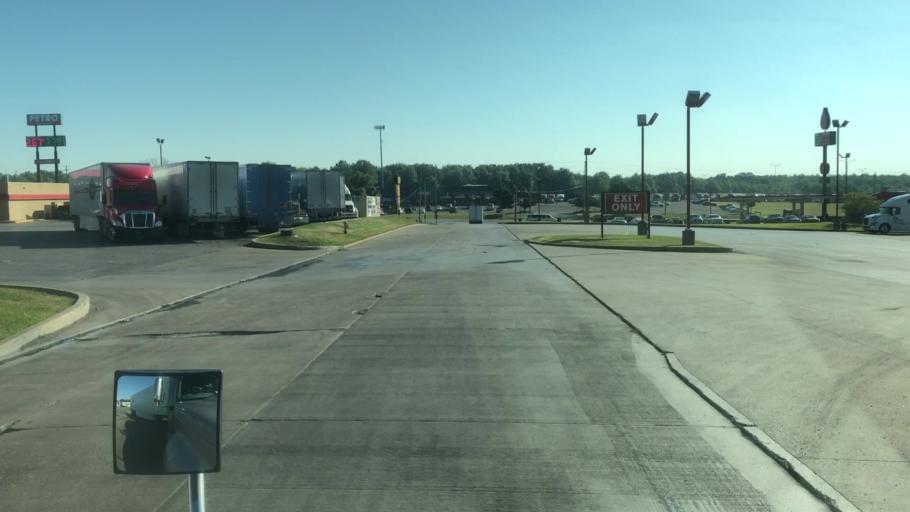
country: US
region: Ohio
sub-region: Trumbull County
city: Girard
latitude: 41.1388
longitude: -80.7196
